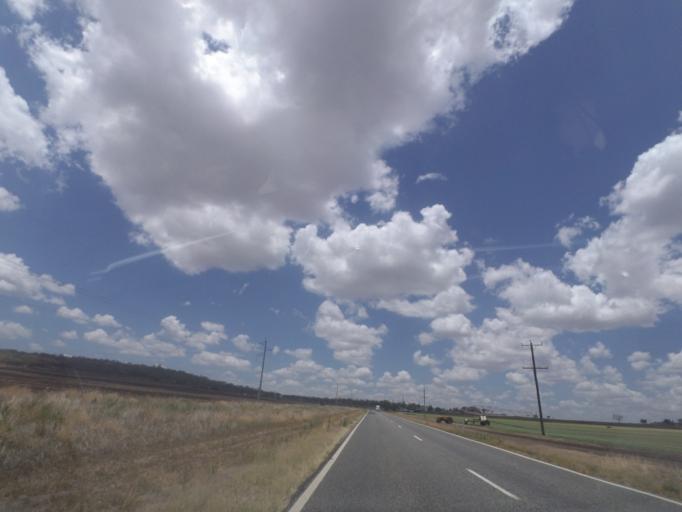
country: AU
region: Queensland
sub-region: Toowoomba
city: Top Camp
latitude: -27.8736
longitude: 151.9638
